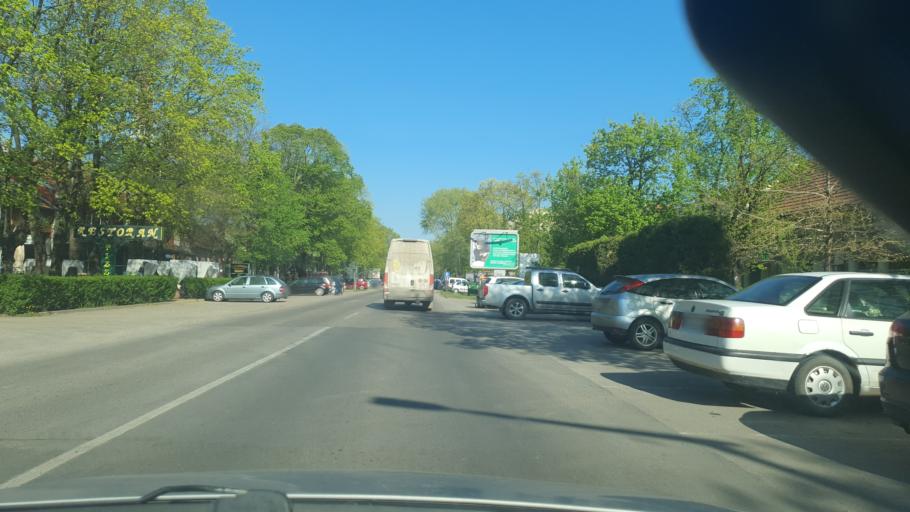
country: RS
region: Autonomna Pokrajina Vojvodina
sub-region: Zapadnobacki Okrug
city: Kula
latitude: 45.6589
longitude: 19.4552
